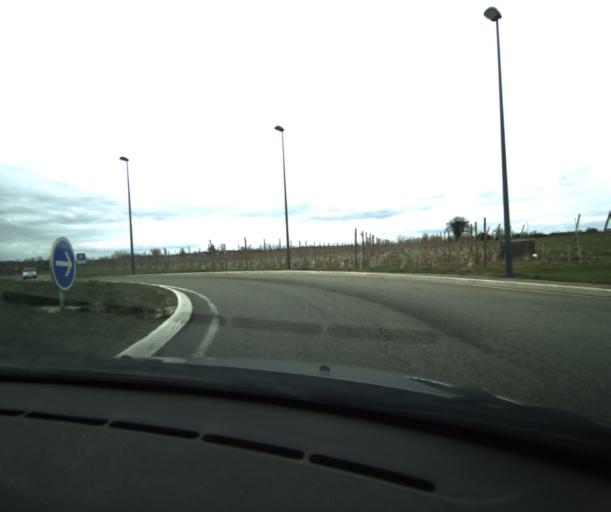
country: FR
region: Midi-Pyrenees
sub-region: Departement du Tarn-et-Garonne
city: Moissac
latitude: 44.0845
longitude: 1.1175
